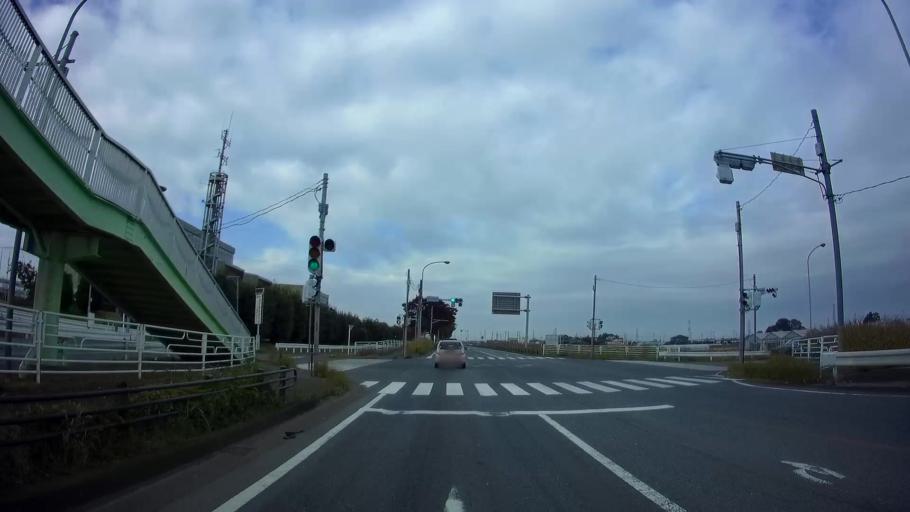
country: JP
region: Saitama
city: Fukayacho
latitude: 36.2123
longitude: 139.2861
